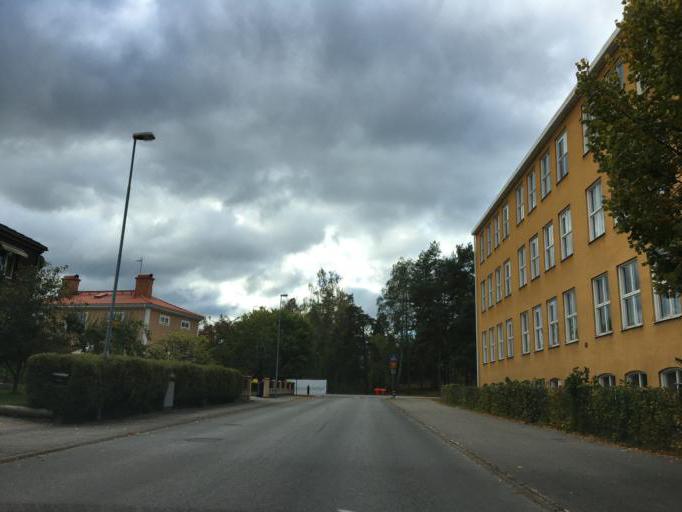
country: SE
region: Soedermanland
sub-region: Katrineholms Kommun
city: Katrineholm
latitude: 58.9890
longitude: 16.2068
